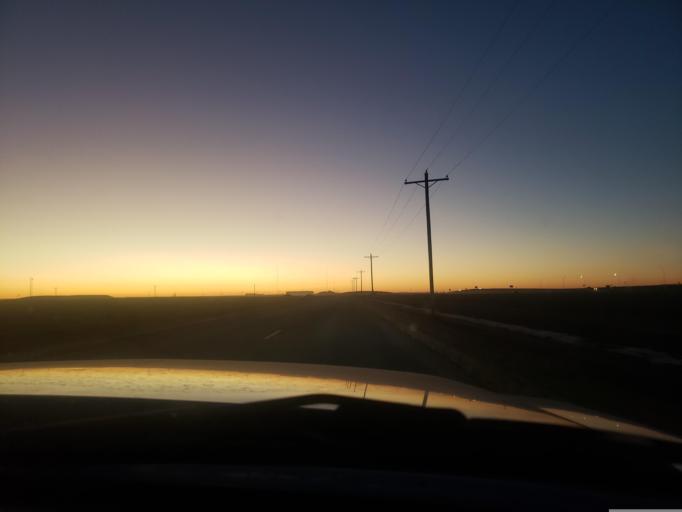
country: US
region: Kansas
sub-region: Finney County
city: Garden City
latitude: 38.0007
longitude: -100.8791
